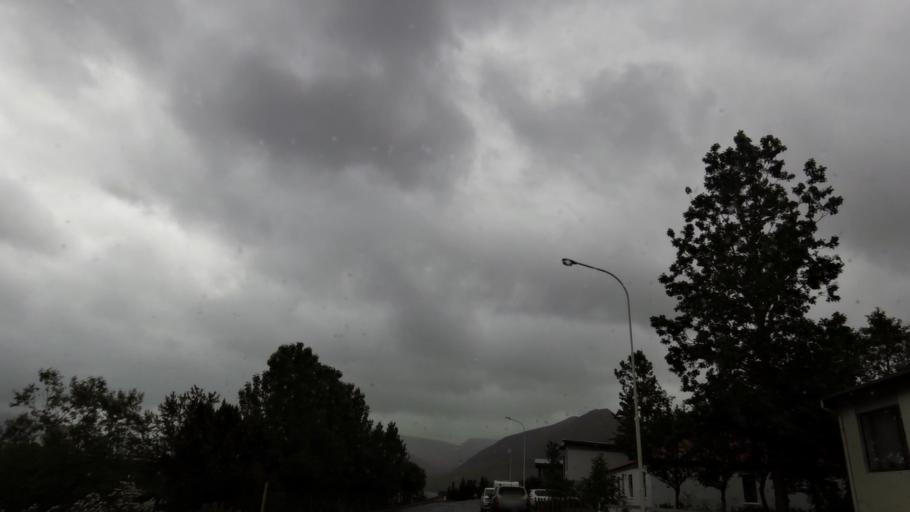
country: IS
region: Westfjords
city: Isafjoerdur
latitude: 65.8726
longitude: -23.4843
